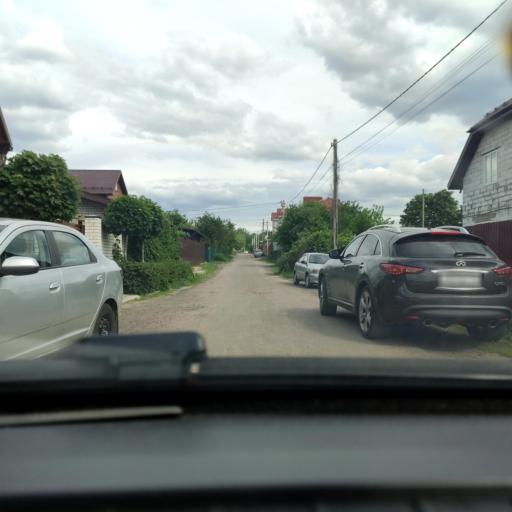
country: RU
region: Voronezj
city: Pridonskoy
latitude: 51.6389
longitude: 39.0828
